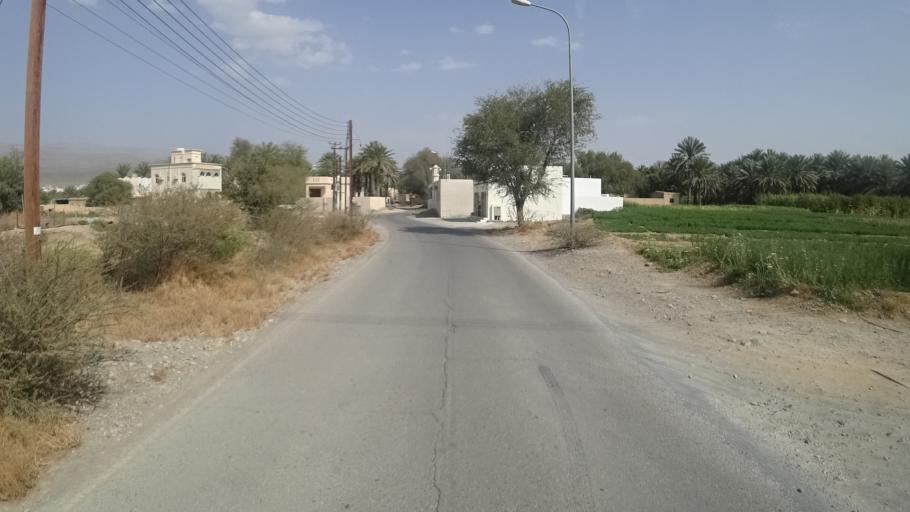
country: OM
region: Muhafazat ad Dakhiliyah
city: Bahla'
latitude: 23.0985
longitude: 57.3028
